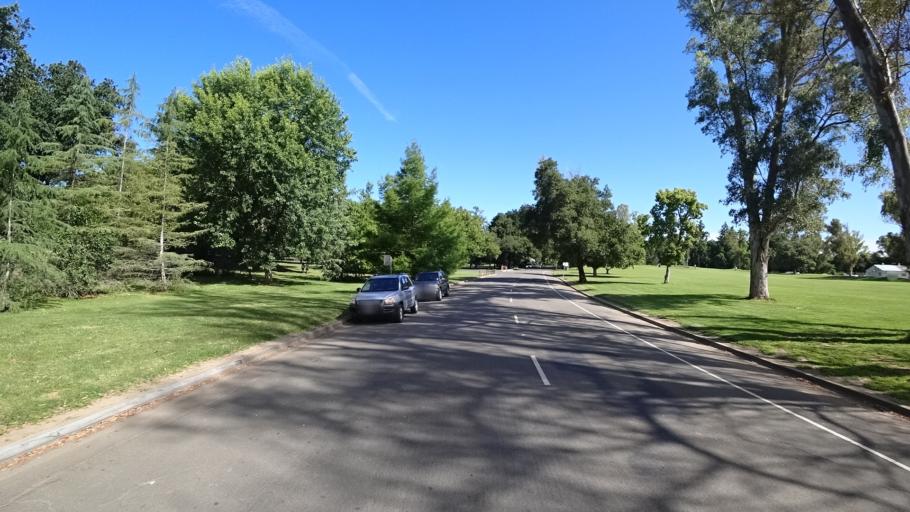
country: US
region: California
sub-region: Sacramento County
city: Sacramento
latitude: 38.5388
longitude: -121.4969
